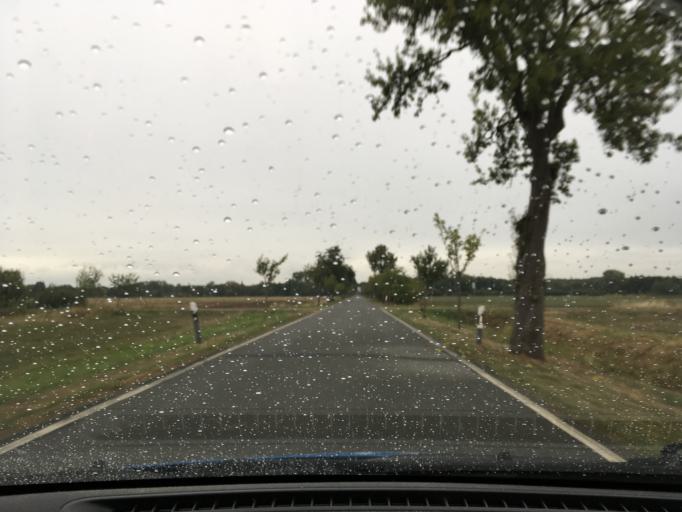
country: DE
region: Lower Saxony
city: Hitzacker
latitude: 53.2182
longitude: 10.9866
